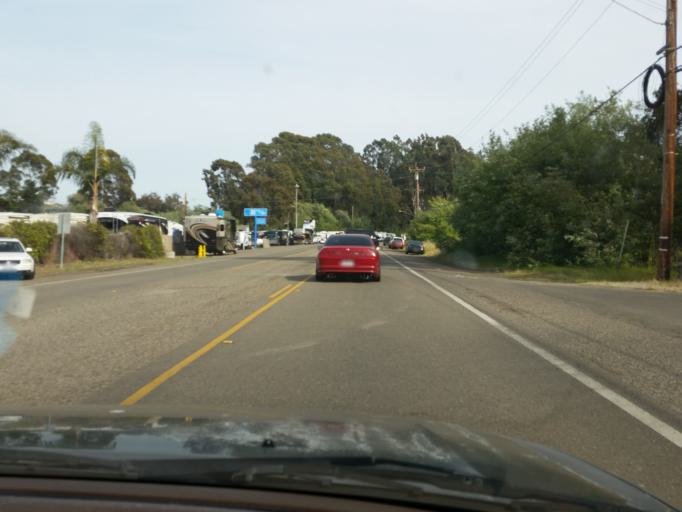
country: US
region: California
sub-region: San Luis Obispo County
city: Pismo Beach
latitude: 35.1324
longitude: -120.6340
